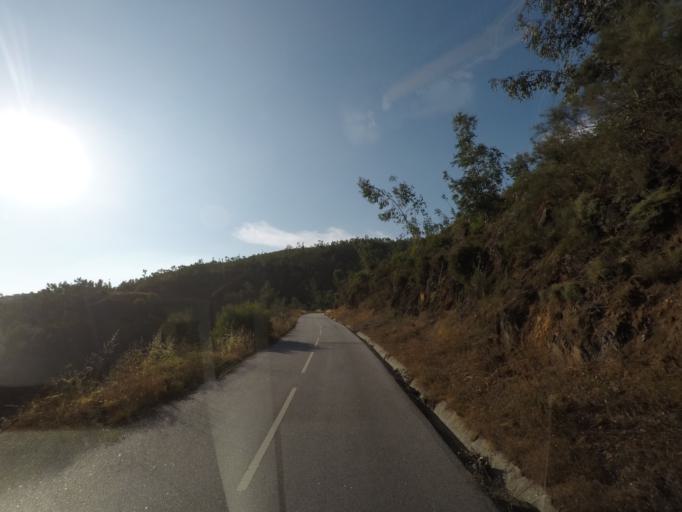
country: PT
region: Vila Real
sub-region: Mesao Frio
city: Mesao Frio
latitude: 41.1641
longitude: -7.9085
